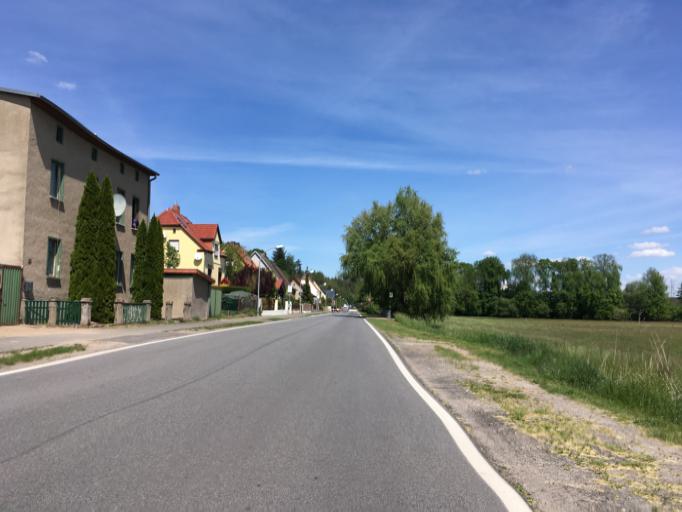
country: DE
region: Brandenburg
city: Niederfinow
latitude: 52.8391
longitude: 13.9372
